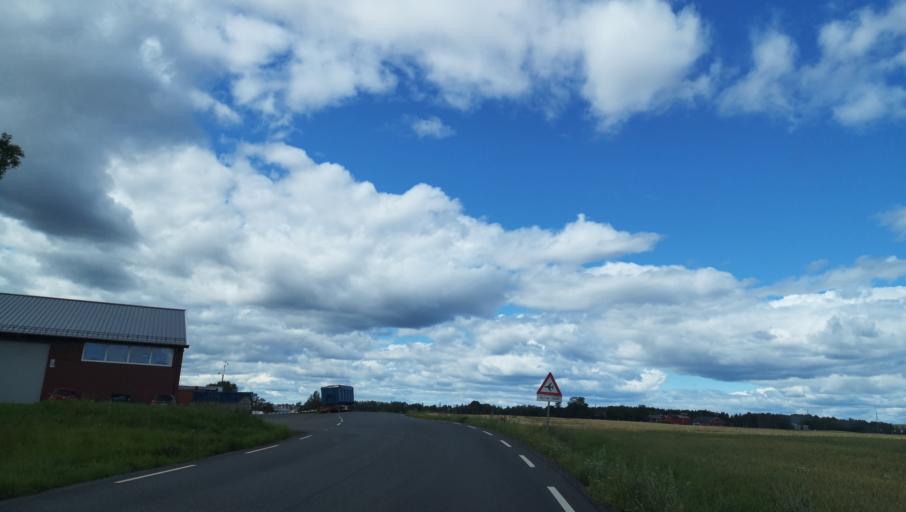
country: NO
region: Akershus
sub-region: Ski
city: Ski
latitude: 59.7088
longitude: 10.8853
